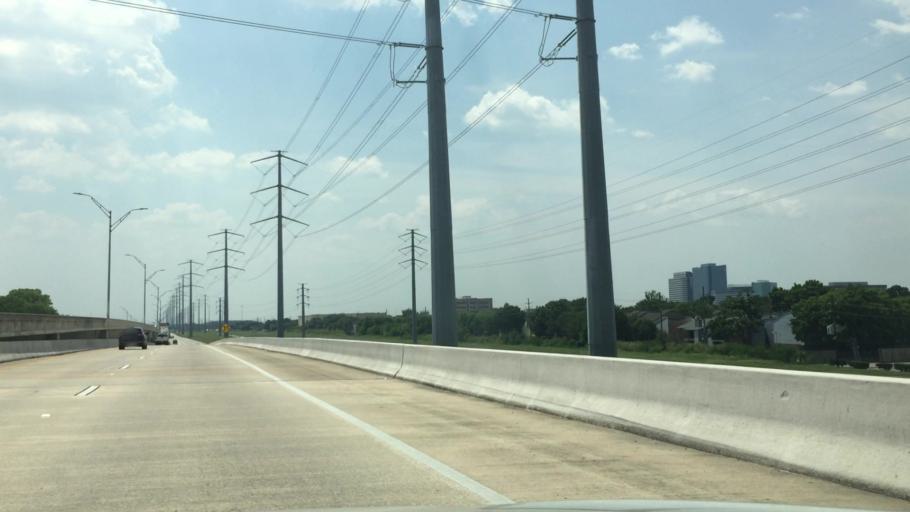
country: US
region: Texas
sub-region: Harris County
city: Piney Point Village
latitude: 29.7198
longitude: -95.5391
